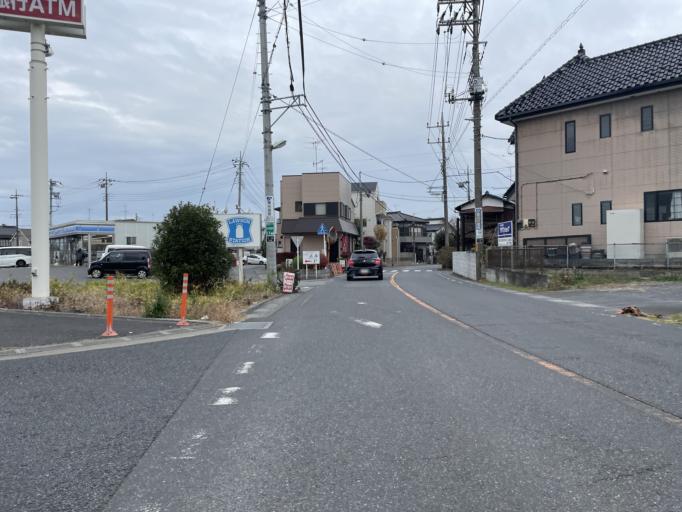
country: JP
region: Saitama
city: Shiraoka
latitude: 36.0138
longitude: 139.6614
